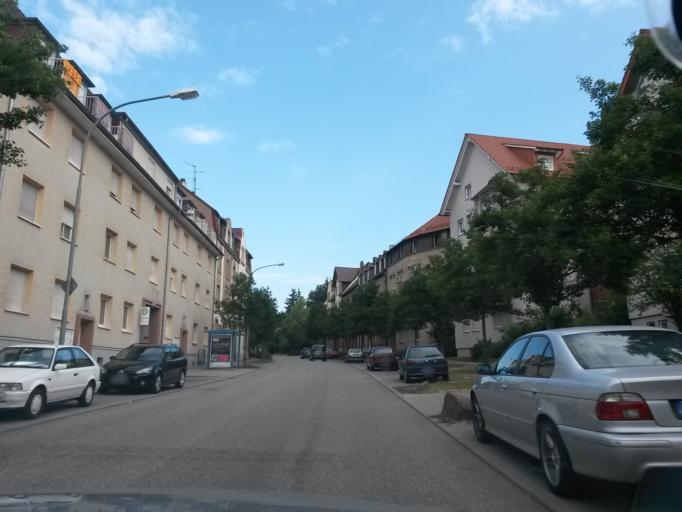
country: DE
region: Baden-Wuerttemberg
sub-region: Karlsruhe Region
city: Ispringen
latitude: 48.8915
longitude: 8.6636
